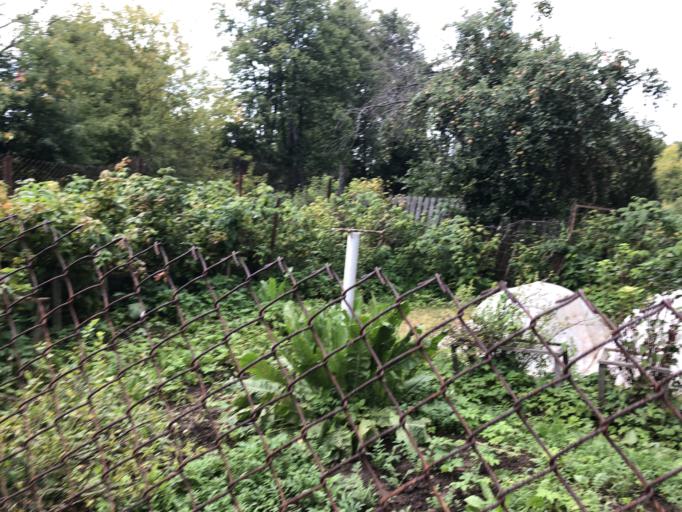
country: RU
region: Moskovskaya
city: Yakhroma
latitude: 56.2957
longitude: 37.4759
